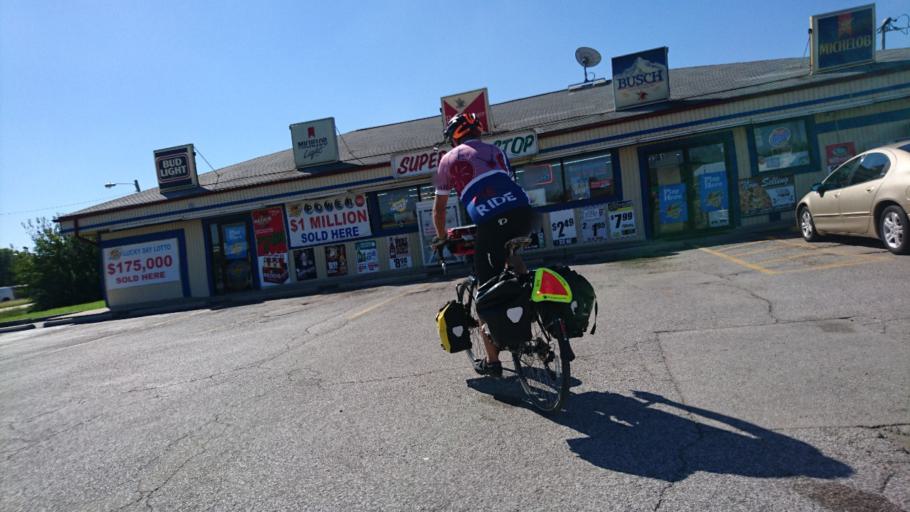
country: US
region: Illinois
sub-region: Madison County
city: Mitchell
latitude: 38.7619
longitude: -90.1251
